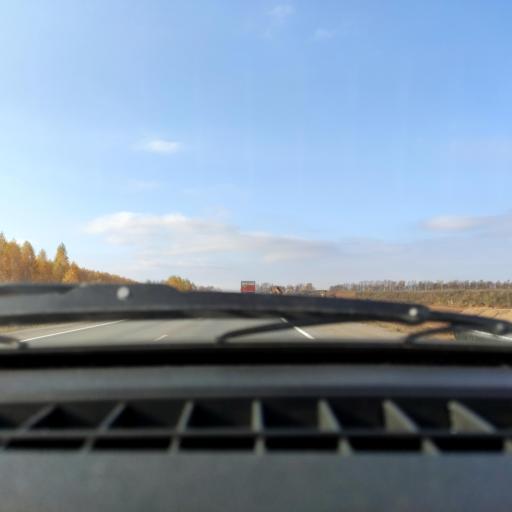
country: RU
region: Bashkortostan
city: Iglino
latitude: 54.7319
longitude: 56.2658
